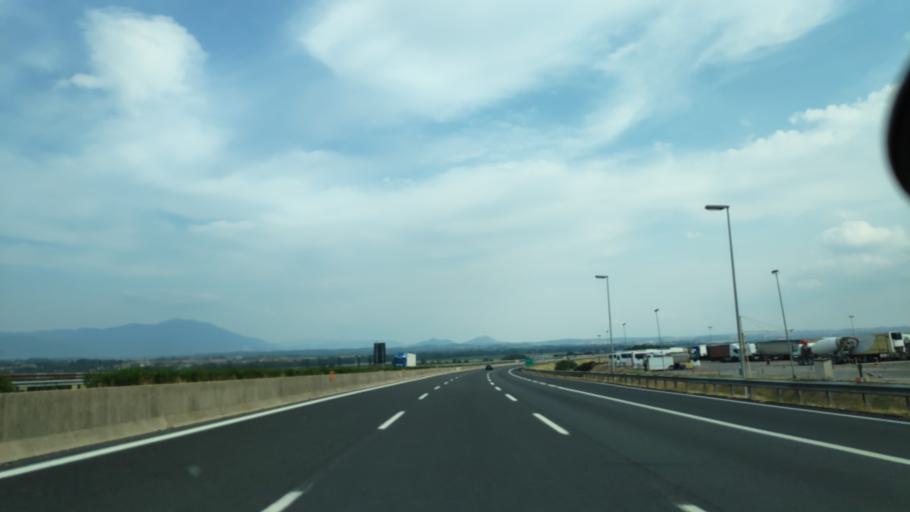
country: IT
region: Latium
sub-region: Citta metropolitana di Roma Capitale
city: Fiano Romano
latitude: 42.1592
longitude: 12.6219
